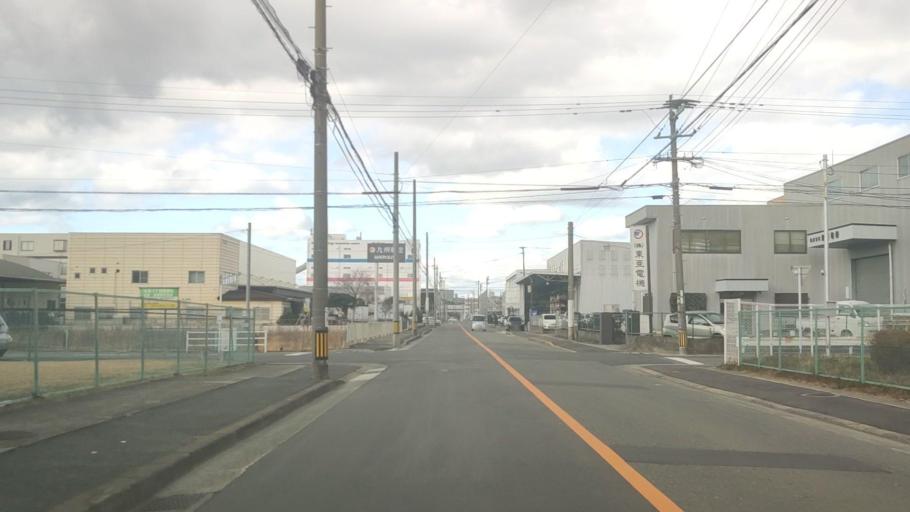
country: JP
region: Fukuoka
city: Fukuoka-shi
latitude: 33.6087
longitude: 130.4357
